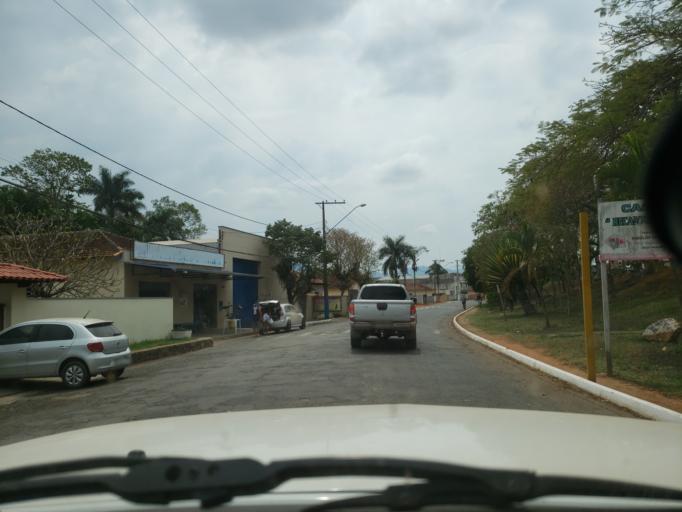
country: BR
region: Minas Gerais
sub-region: Jacutinga
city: Jacutinga
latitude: -22.2778
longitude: -46.6061
